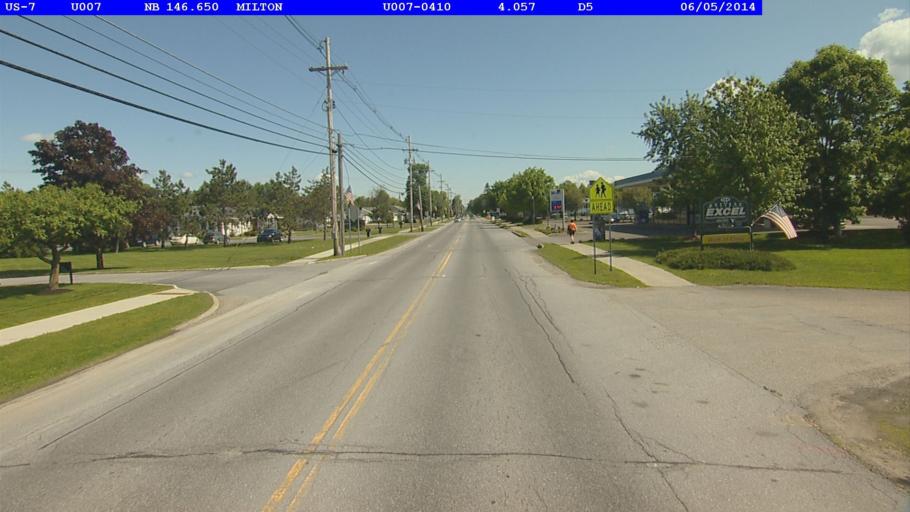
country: US
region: Vermont
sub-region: Chittenden County
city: Milton
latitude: 44.6261
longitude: -73.1174
